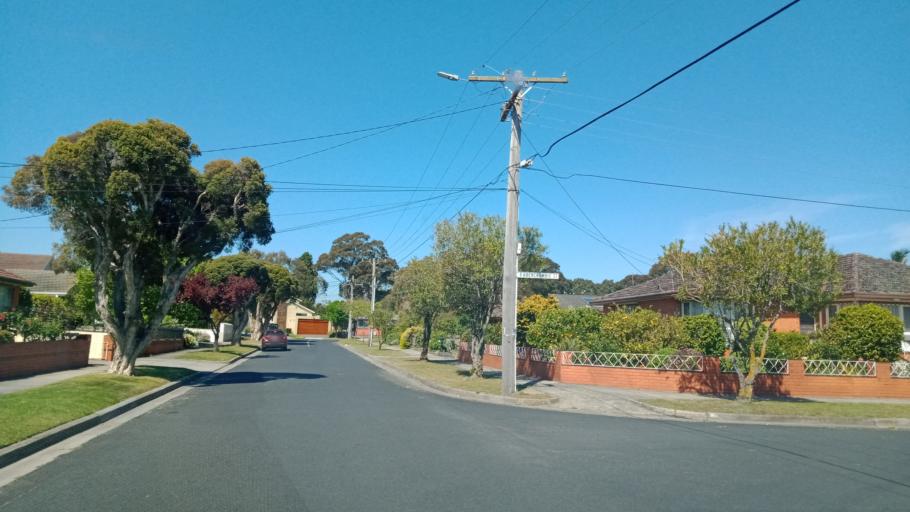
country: AU
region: Victoria
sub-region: Monash
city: Oakleigh South
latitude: -37.9299
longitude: 145.0832
